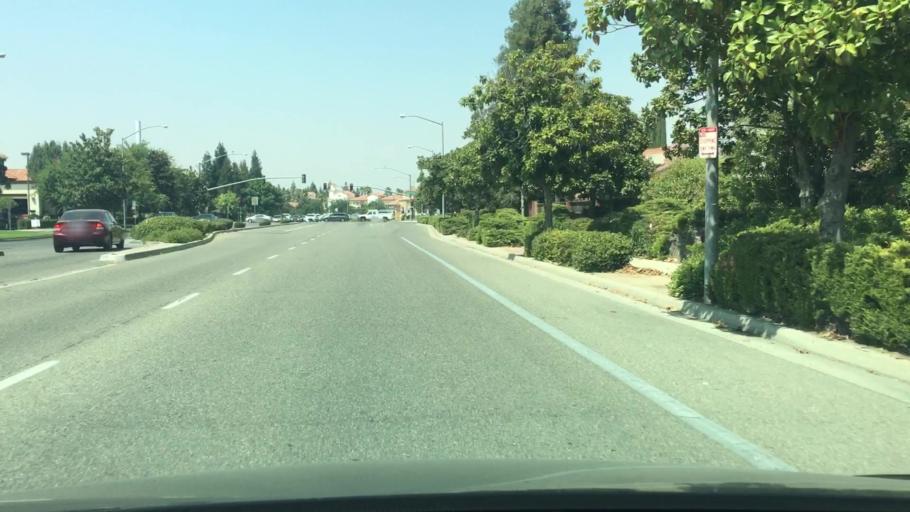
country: US
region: California
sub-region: Fresno County
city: Clovis
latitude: 36.8651
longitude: -119.7567
